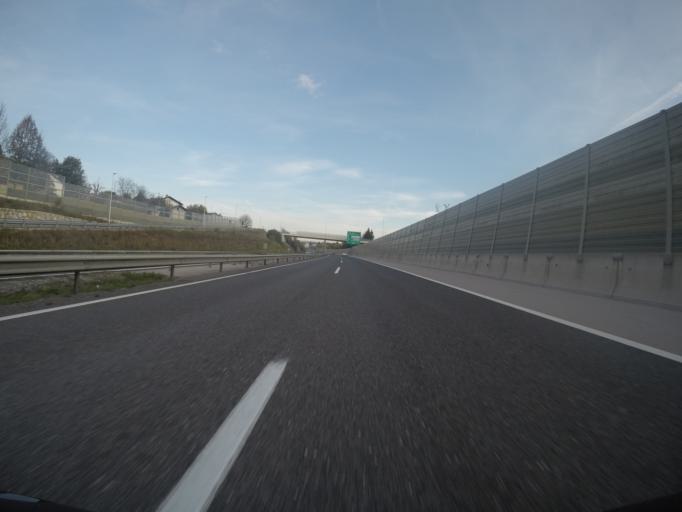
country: SI
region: Grosuplje
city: Smarje-Sap
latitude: 45.9792
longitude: 14.6047
